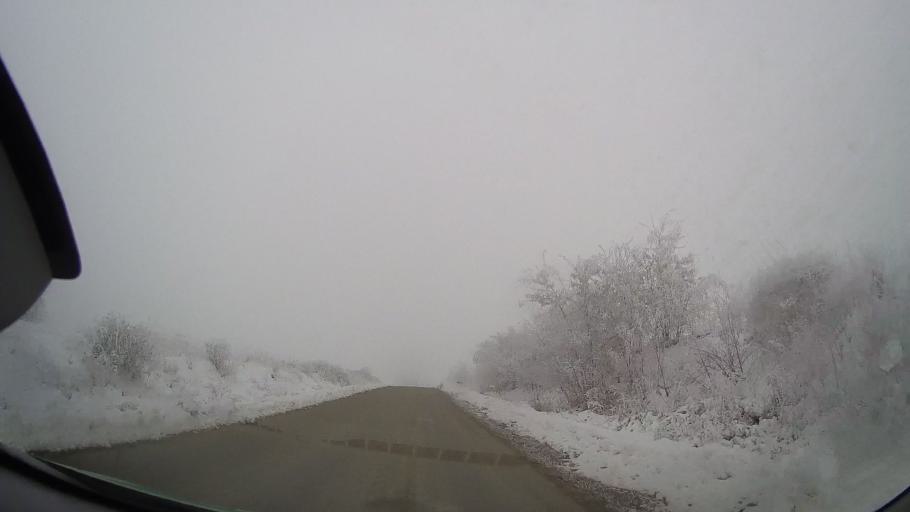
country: RO
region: Iasi
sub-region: Comuna Tansa
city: Suhulet
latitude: 46.8871
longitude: 27.2713
